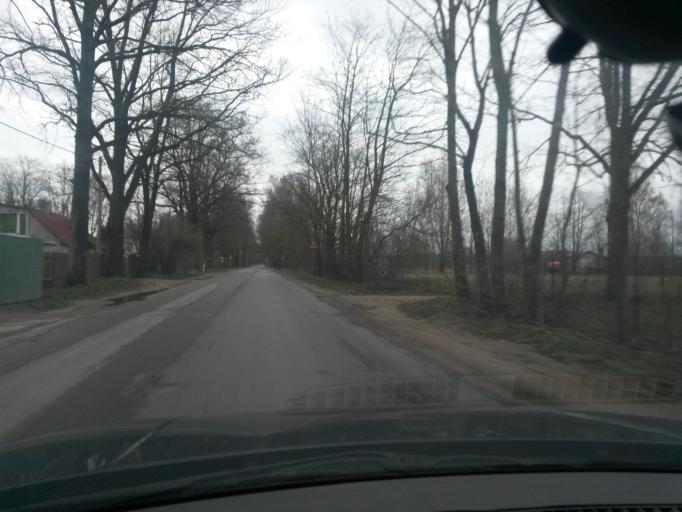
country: LV
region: Kekava
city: Kekava
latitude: 56.8954
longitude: 24.2362
